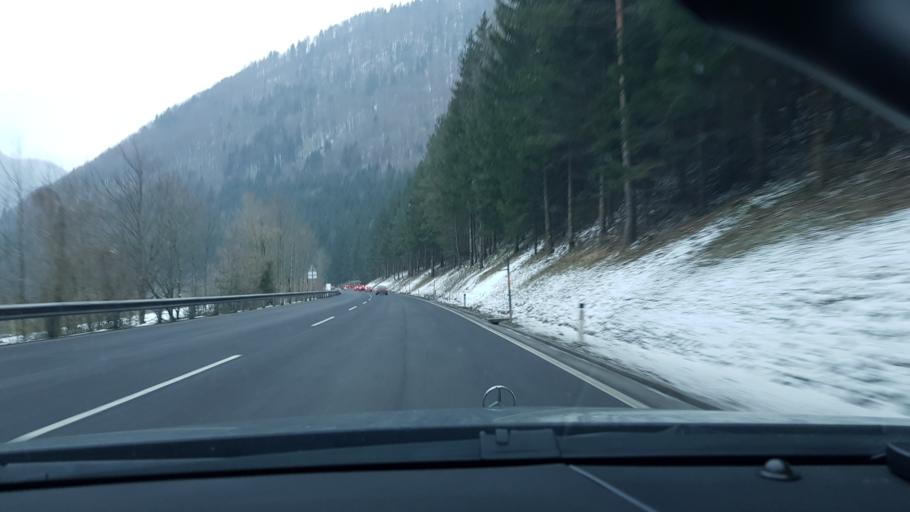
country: AT
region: Lower Austria
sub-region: Politischer Bezirk Scheibbs
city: Gaming
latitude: 47.9030
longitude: 15.0695
